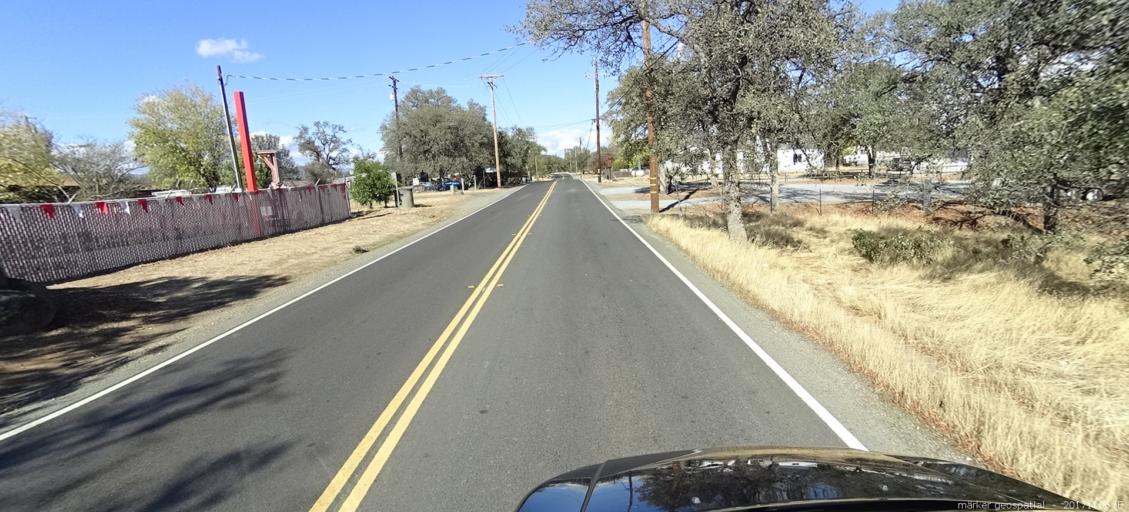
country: US
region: California
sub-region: Shasta County
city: Palo Cedro
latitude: 40.5672
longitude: -122.2992
